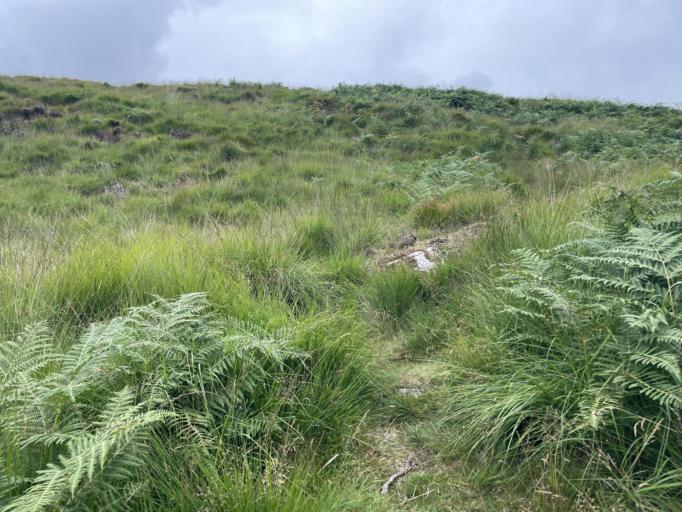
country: GB
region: Scotland
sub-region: Dumfries and Galloway
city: Newton Stewart
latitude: 54.9520
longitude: -4.2649
